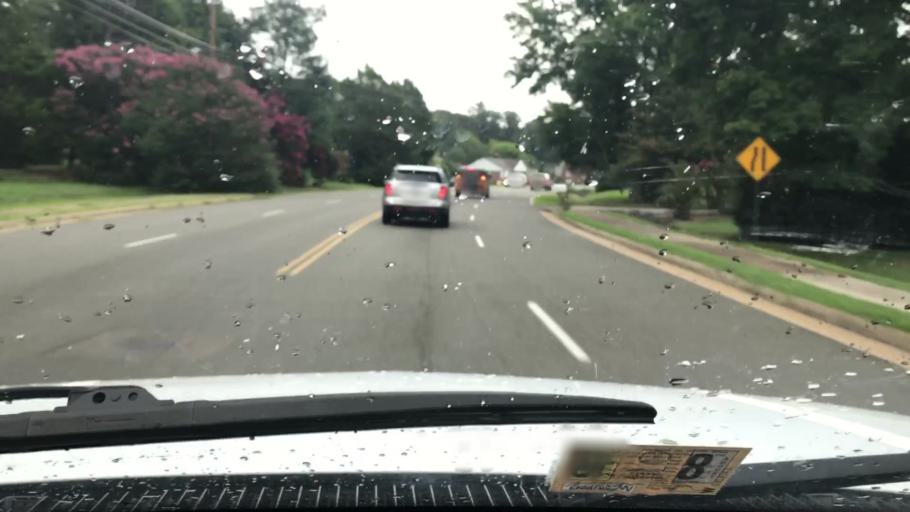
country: US
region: Virginia
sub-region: Henrico County
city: Dumbarton
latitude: 37.6015
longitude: -77.4980
